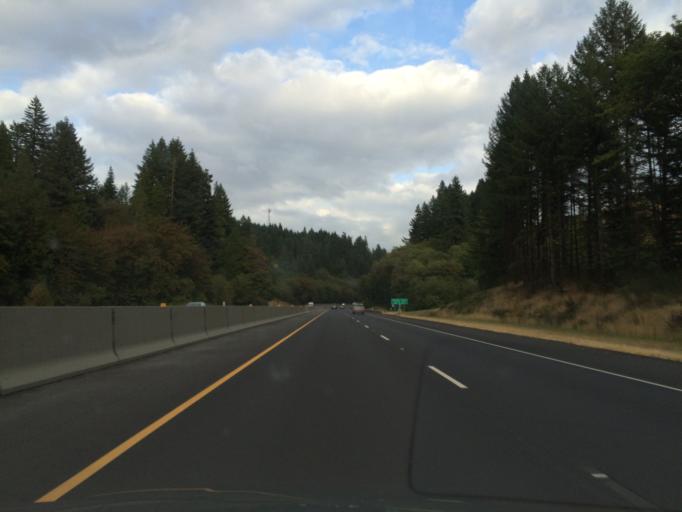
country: US
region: Oregon
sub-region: Lane County
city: Cottage Grove
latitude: 43.7527
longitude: -123.1587
